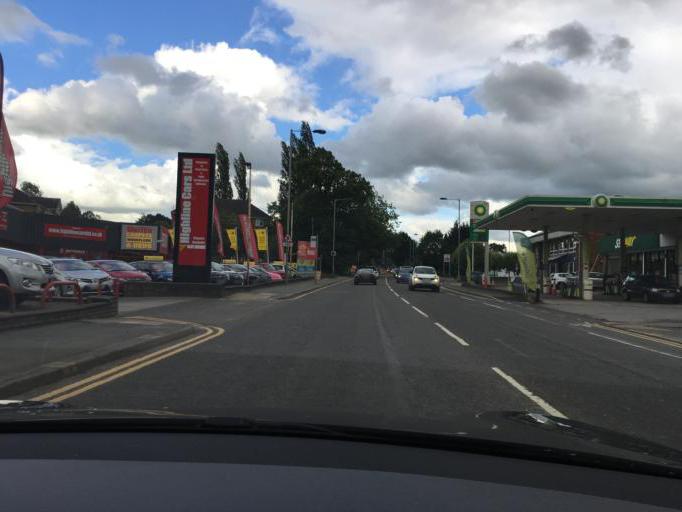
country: GB
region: England
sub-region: Borough of Stockport
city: Hazel Grove
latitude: 53.3739
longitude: -2.1092
